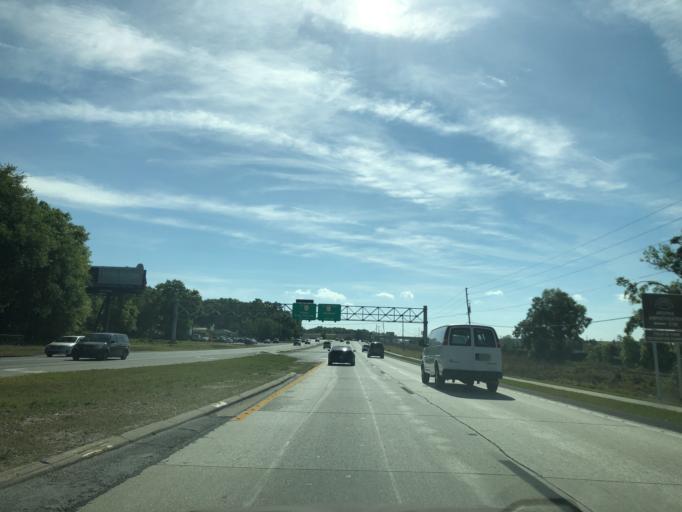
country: US
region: Florida
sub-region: Orange County
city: Zellwood
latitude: 28.6977
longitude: -81.5668
